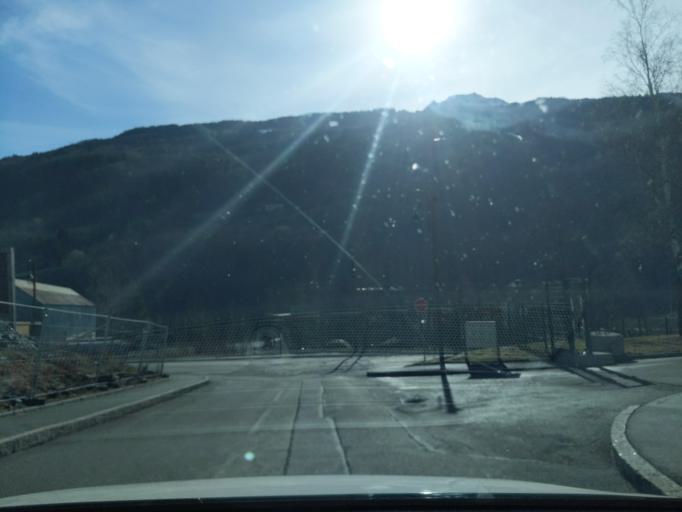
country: FR
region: Rhone-Alpes
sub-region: Departement de la Savoie
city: Bourg-Saint-Maurice
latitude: 45.6105
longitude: 6.7696
